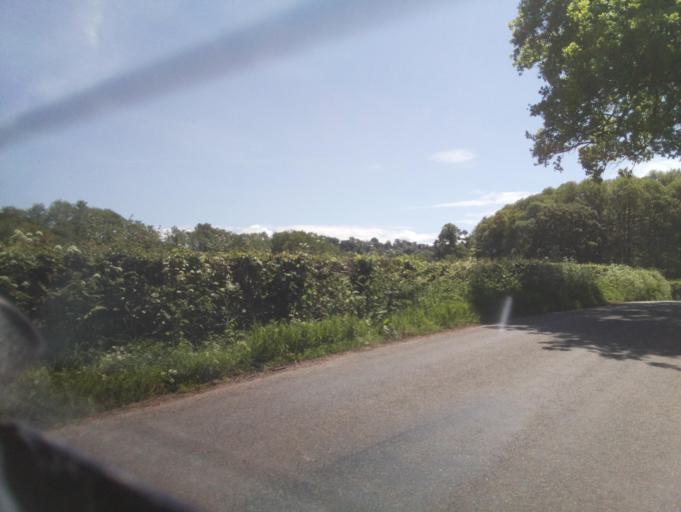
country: GB
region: Wales
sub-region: Monmouthshire
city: Caldicot
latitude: 51.6519
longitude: -2.7561
